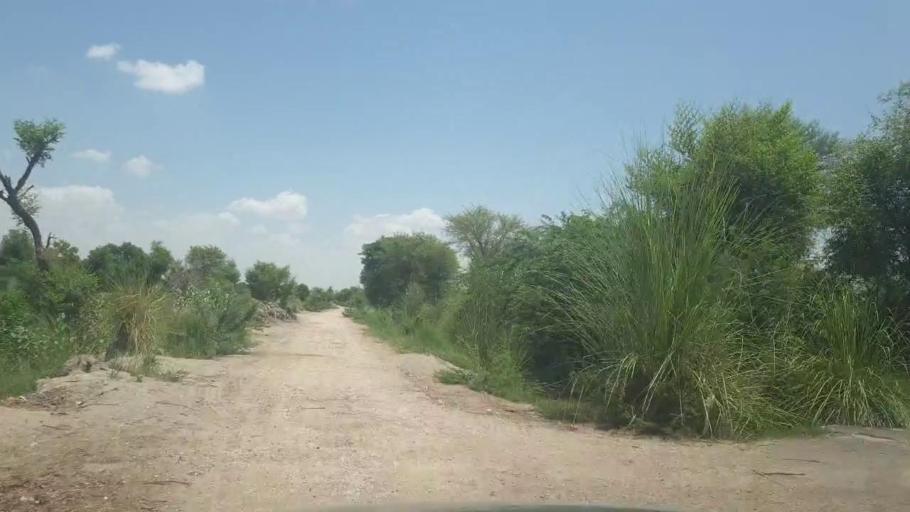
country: PK
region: Sindh
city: Kot Diji
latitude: 27.2634
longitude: 69.0216
